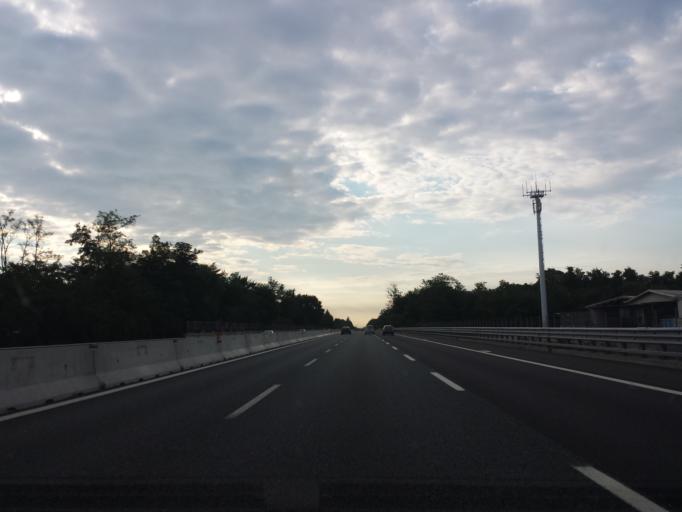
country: IT
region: Lombardy
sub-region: Provincia di Varese
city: Olgiate Olona
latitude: 45.6328
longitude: 8.8744
